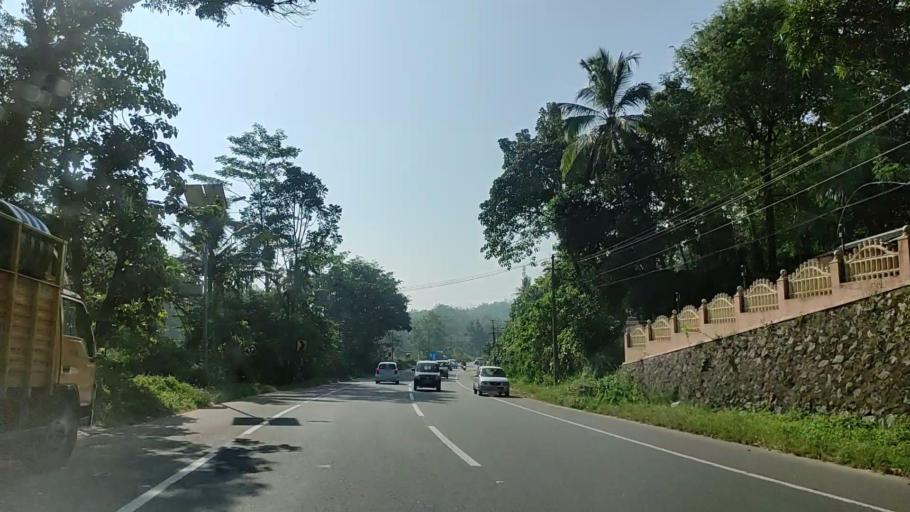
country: IN
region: Kerala
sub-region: Kollam
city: Punalur
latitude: 8.9117
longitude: 76.8544
